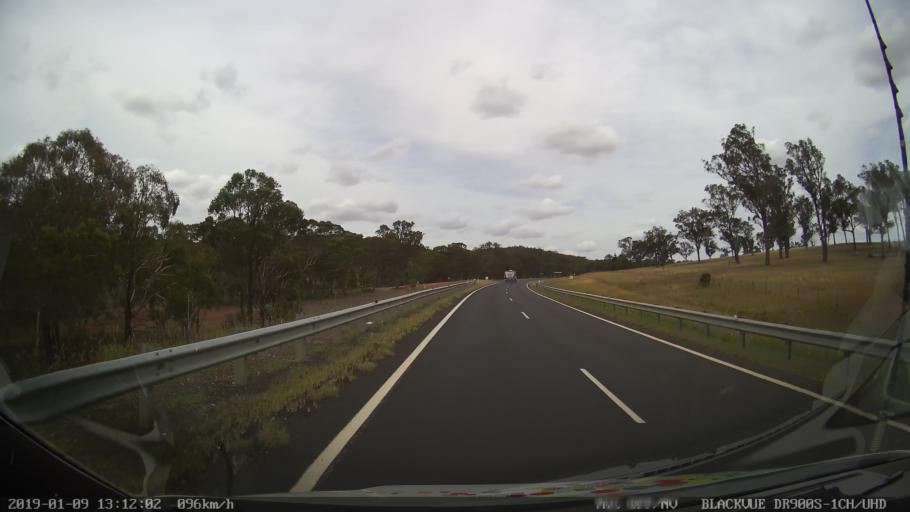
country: AU
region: New South Wales
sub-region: Armidale Dumaresq
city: Armidale
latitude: -30.5395
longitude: 151.7341
